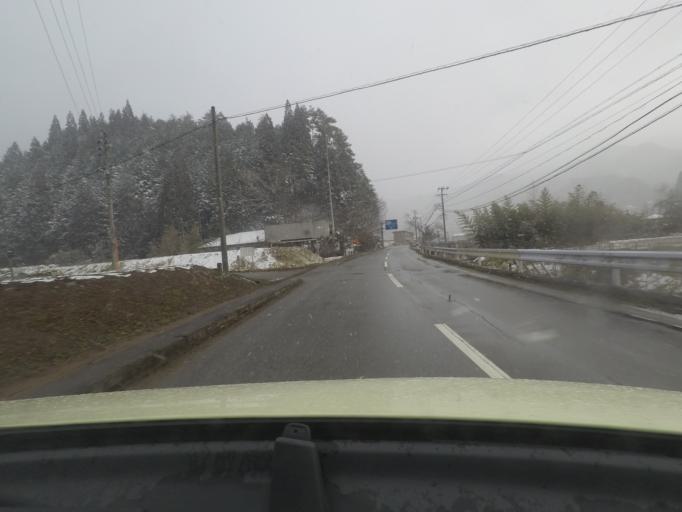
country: JP
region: Gifu
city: Takayama
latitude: 36.1401
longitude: 137.3115
